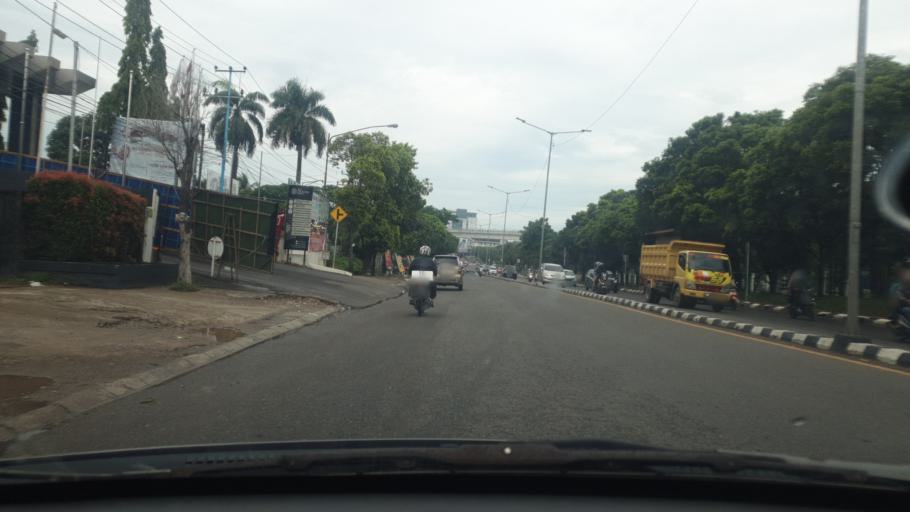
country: ID
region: South Sumatra
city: Palembang
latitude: -2.9713
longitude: 104.7307
